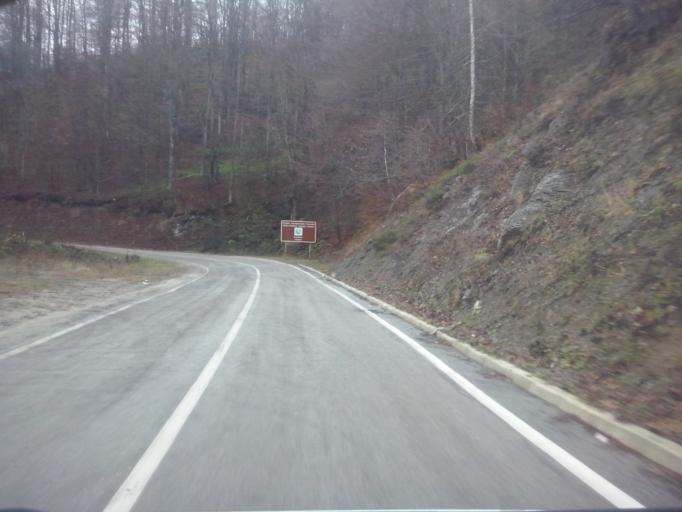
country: RS
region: Central Serbia
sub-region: Moravicki Okrug
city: Ivanjica
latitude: 43.5284
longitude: 20.3306
